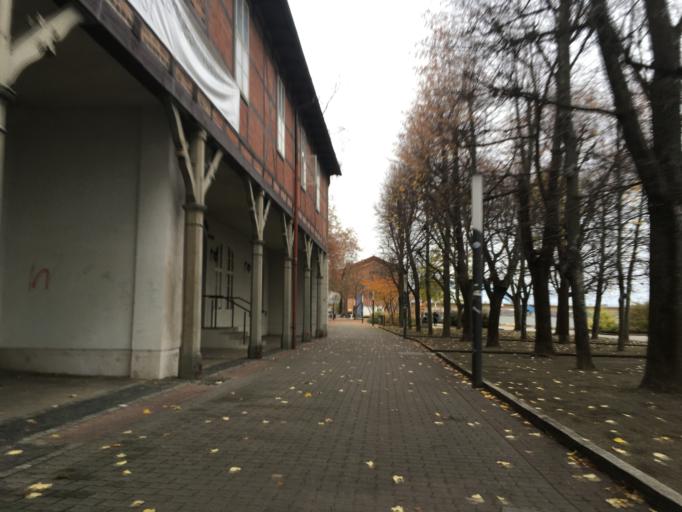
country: DE
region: Brandenburg
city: Frankfurt (Oder)
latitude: 52.3453
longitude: 14.5569
